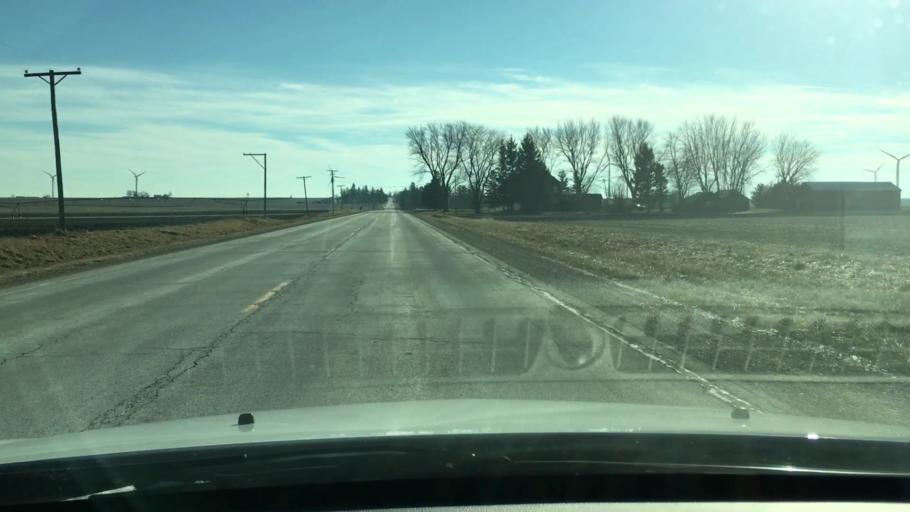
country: US
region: Illinois
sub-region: LaSalle County
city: Mendota
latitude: 41.6477
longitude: -89.1296
